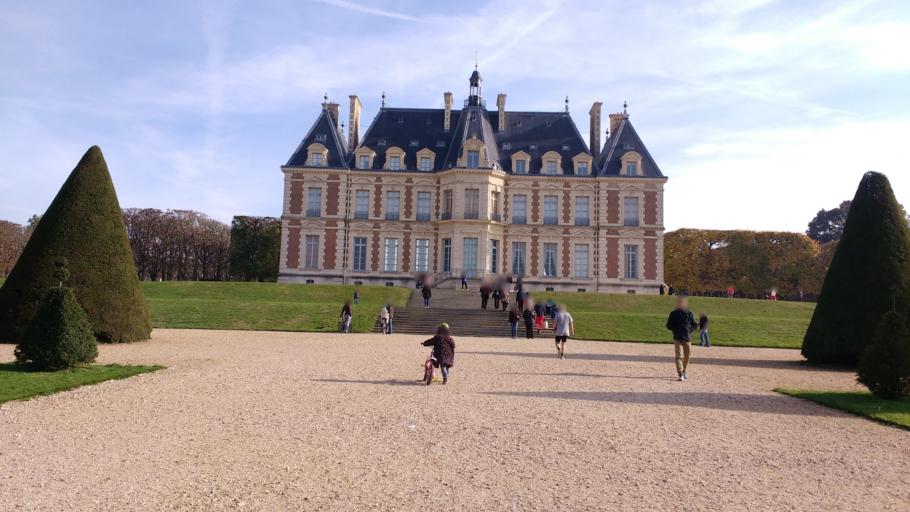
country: FR
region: Ile-de-France
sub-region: Departement des Hauts-de-Seine
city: Sceaux
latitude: 48.7742
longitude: 2.2990
